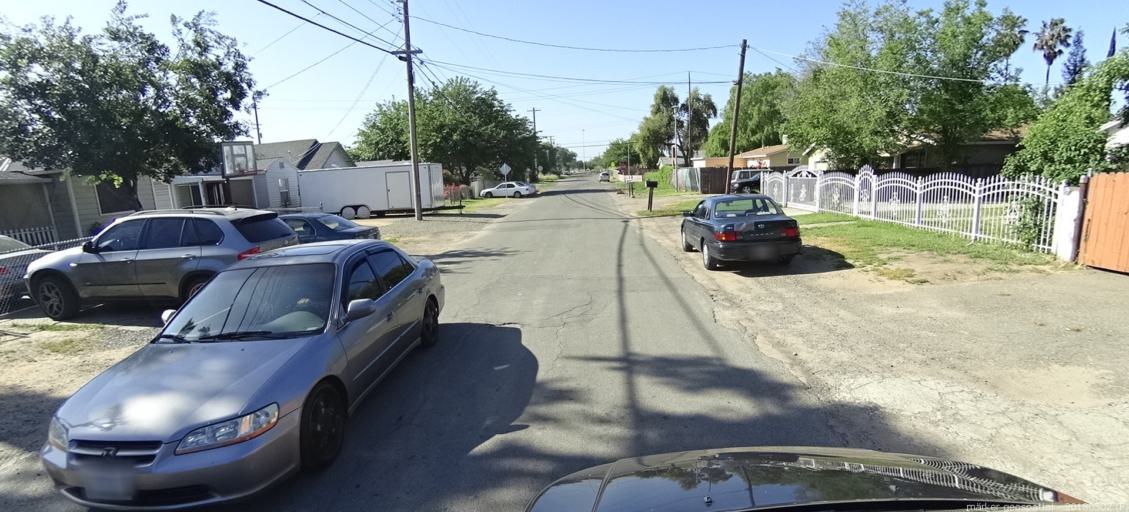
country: US
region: California
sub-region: Sacramento County
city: Arden-Arcade
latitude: 38.6155
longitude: -121.4254
